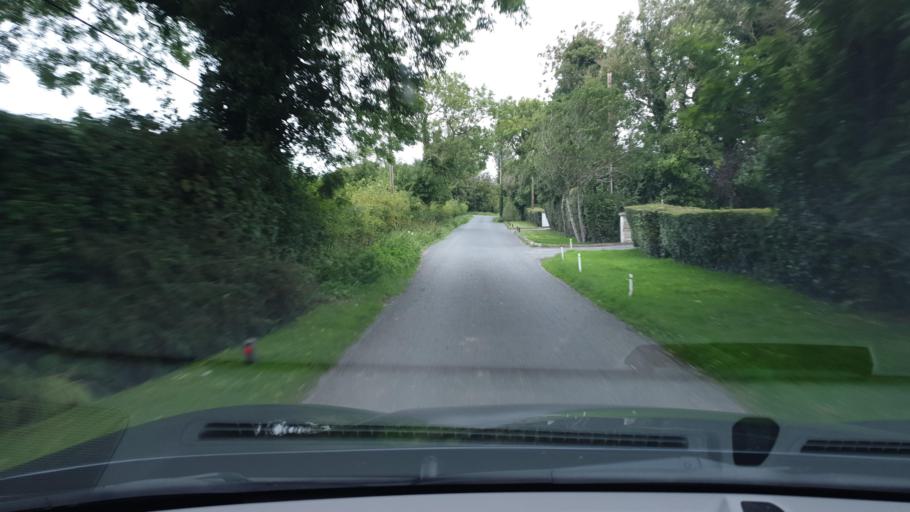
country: IE
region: Leinster
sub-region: An Mhi
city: Ratoath
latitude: 53.5036
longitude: -6.4877
